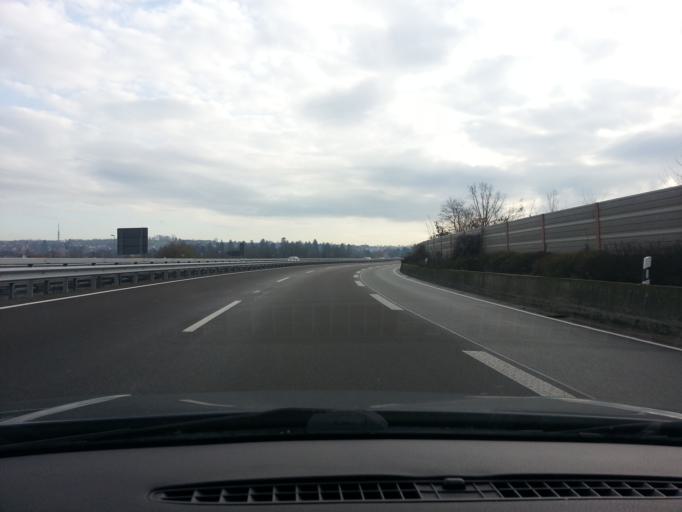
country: DE
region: Rheinland-Pfalz
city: Zweibrucken
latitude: 49.2458
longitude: 7.3573
